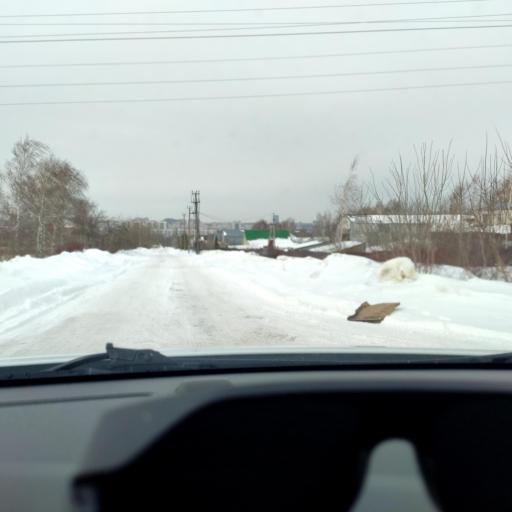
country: RU
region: Tatarstan
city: Vysokaya Gora
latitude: 55.8000
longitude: 49.2807
